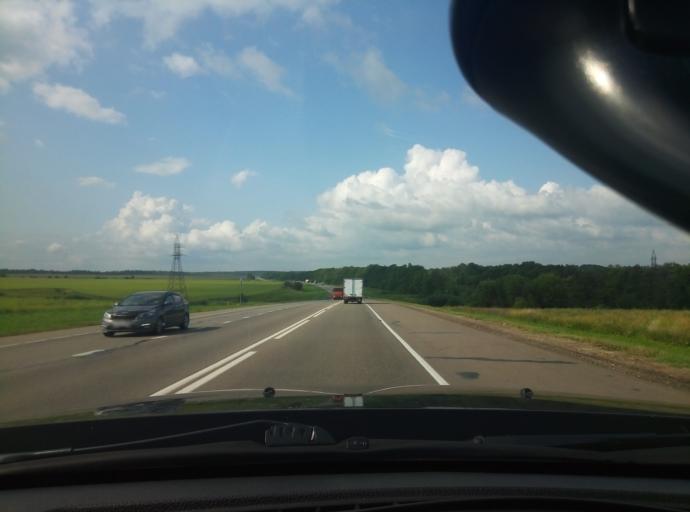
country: RU
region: Tula
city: Shchekino
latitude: 53.9576
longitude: 37.4853
